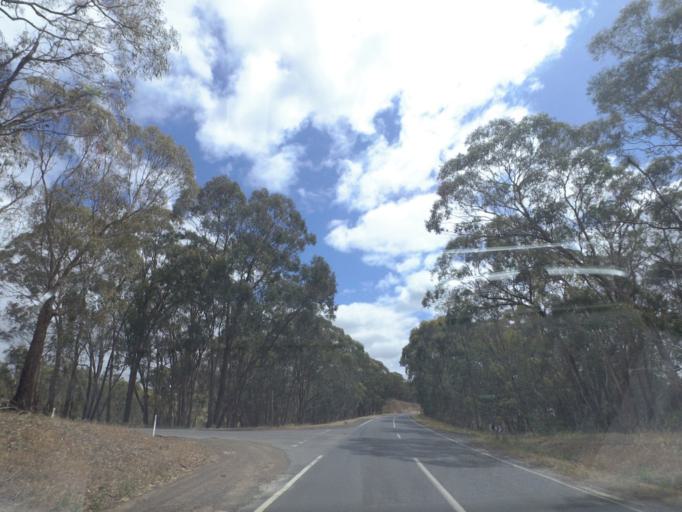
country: AU
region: Victoria
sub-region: Whittlesea
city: Whittlesea
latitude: -37.2447
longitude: 145.0449
